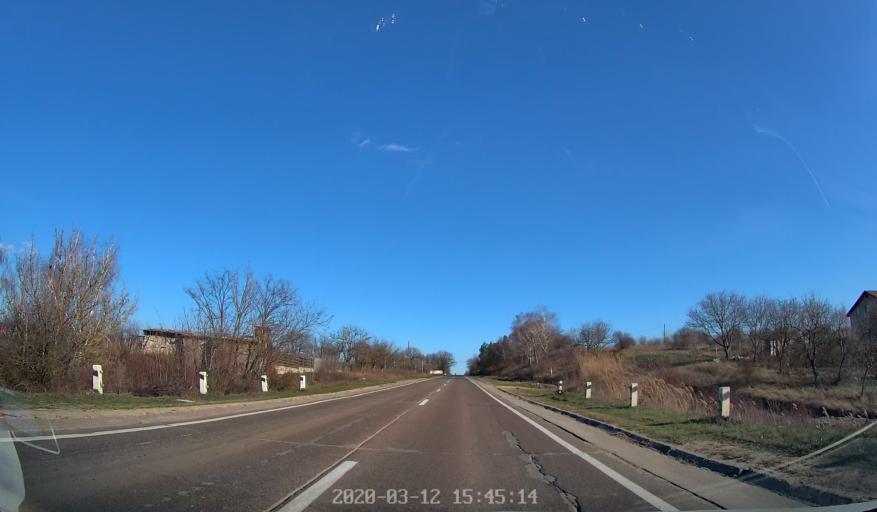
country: MD
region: Chisinau
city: Stauceni
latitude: 47.1070
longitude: 28.8722
